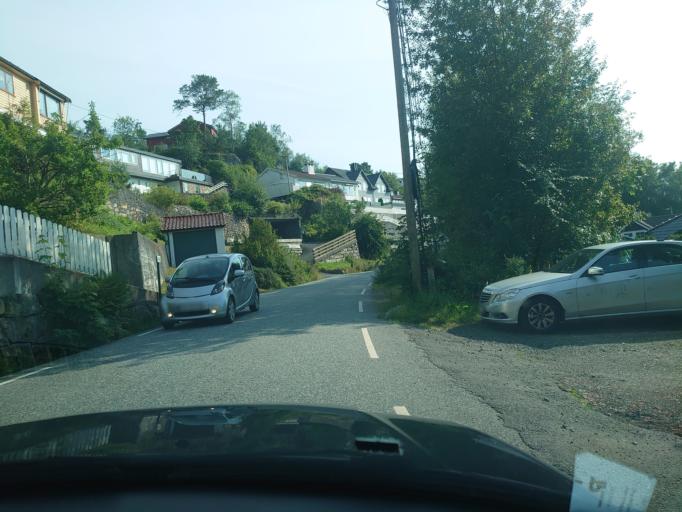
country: NO
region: Hordaland
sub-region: Bergen
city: Ytrebygda
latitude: 60.3363
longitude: 5.2851
